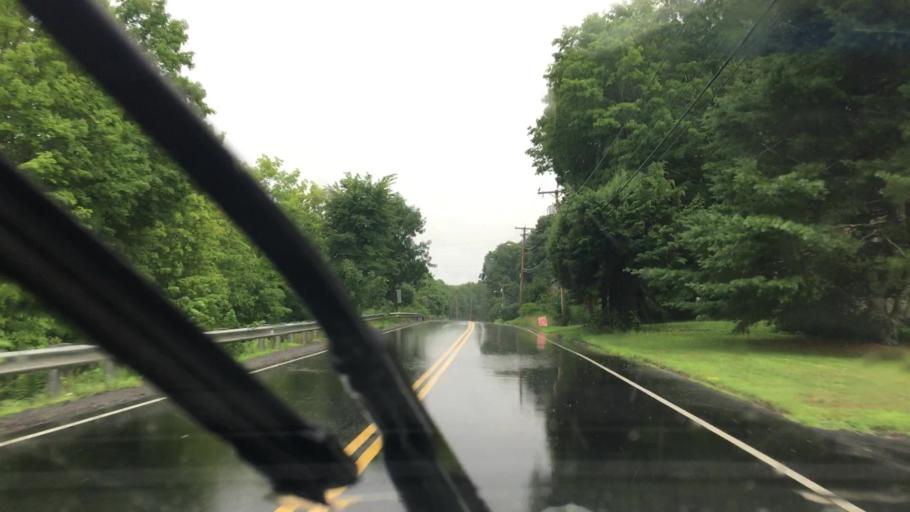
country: US
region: Maine
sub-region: Kennebec County
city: Randolph
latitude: 44.2220
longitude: -69.7649
